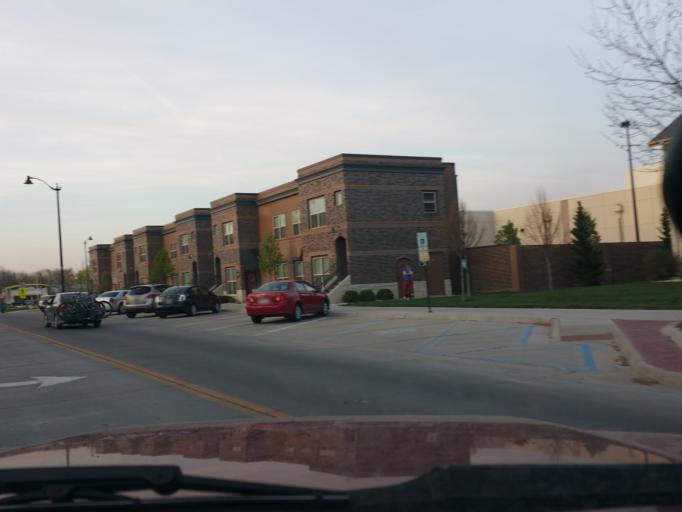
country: US
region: Kansas
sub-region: Riley County
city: Manhattan
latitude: 39.1846
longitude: -96.5618
